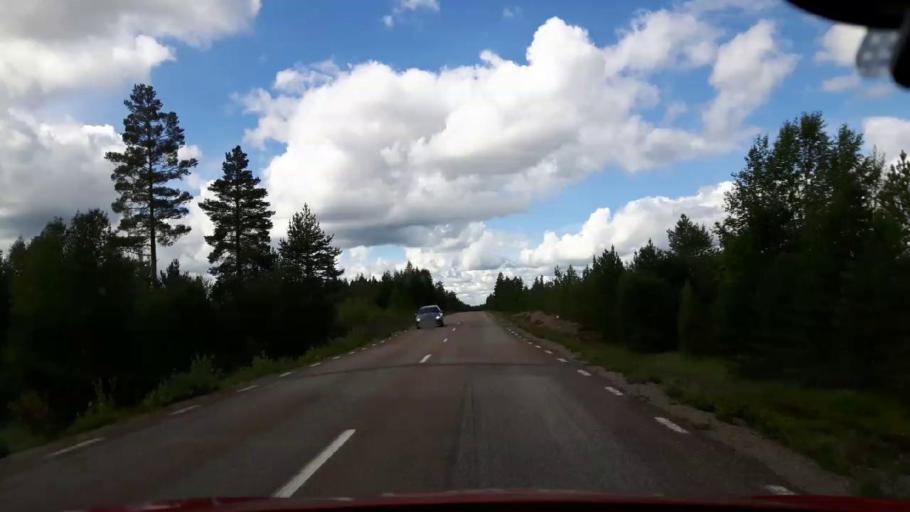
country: SE
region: Jaemtland
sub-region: Harjedalens Kommun
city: Sveg
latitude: 61.8399
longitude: 14.0160
